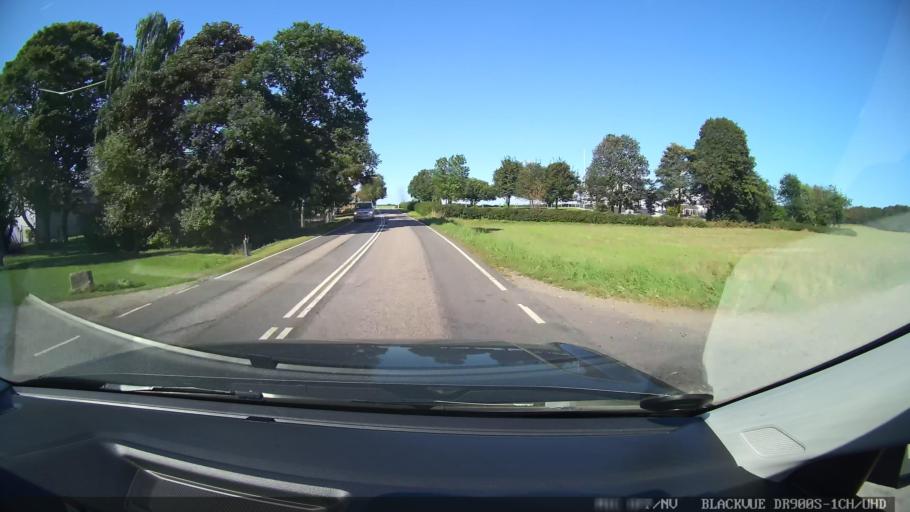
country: DK
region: Central Jutland
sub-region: Randers Kommune
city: Spentrup
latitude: 56.5684
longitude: 9.9984
